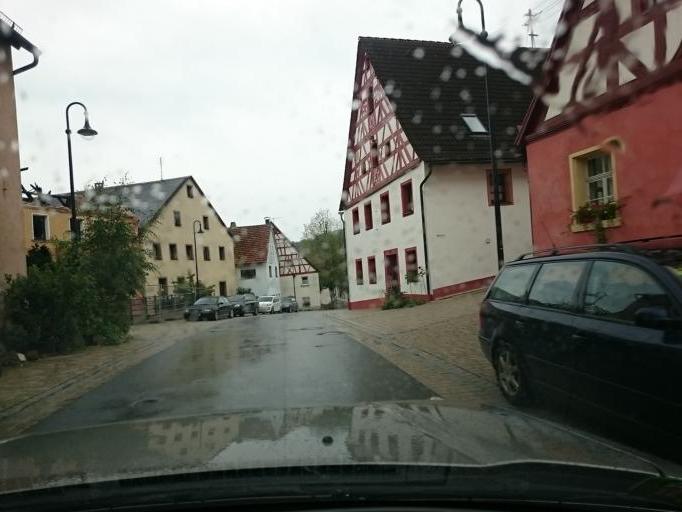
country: DE
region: Bavaria
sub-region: Upper Franconia
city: Obertrubach
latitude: 49.6821
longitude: 11.4181
